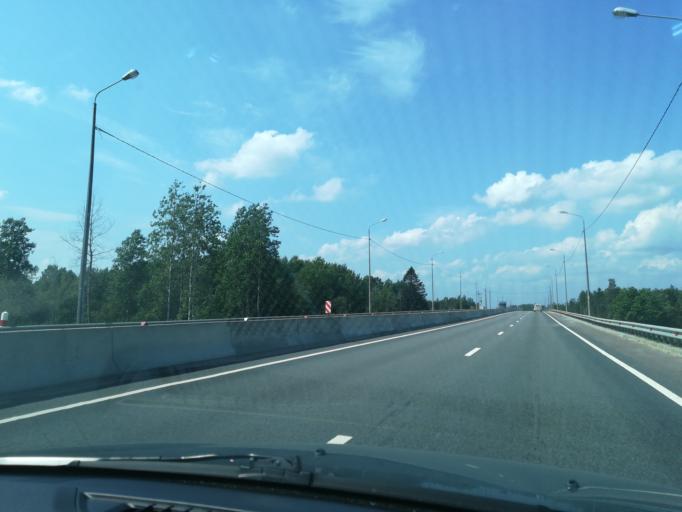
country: RU
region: Leningrad
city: Kingisepp
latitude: 59.5963
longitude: 28.7290
